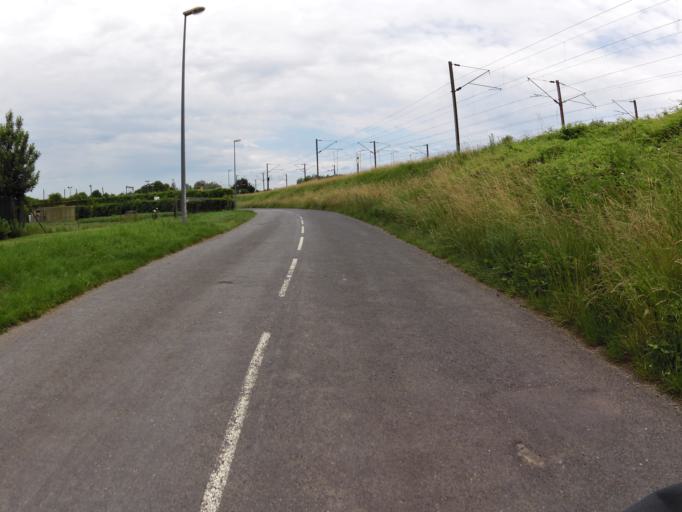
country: FR
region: Champagne-Ardenne
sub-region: Departement des Ardennes
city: Lumes
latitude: 49.7332
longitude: 4.7824
